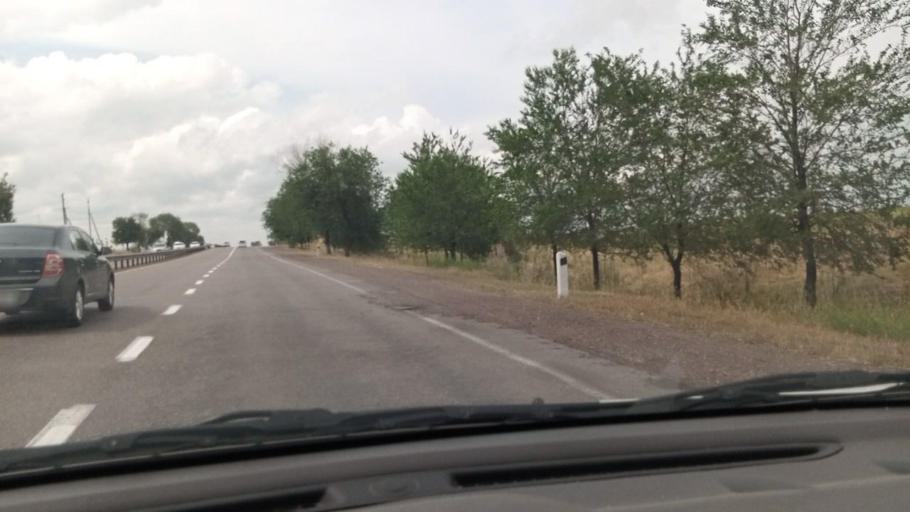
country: UZ
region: Toshkent
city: Tuytepa
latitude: 41.0141
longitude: 69.5170
